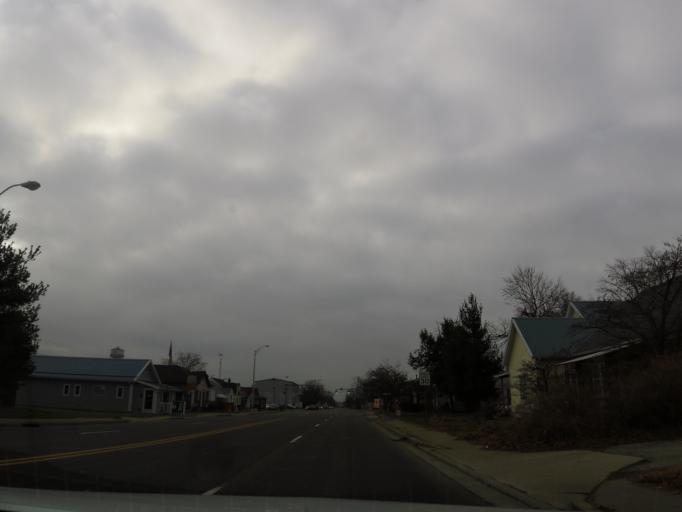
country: US
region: Indiana
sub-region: Bartholomew County
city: Columbus
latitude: 39.2174
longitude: -85.9042
